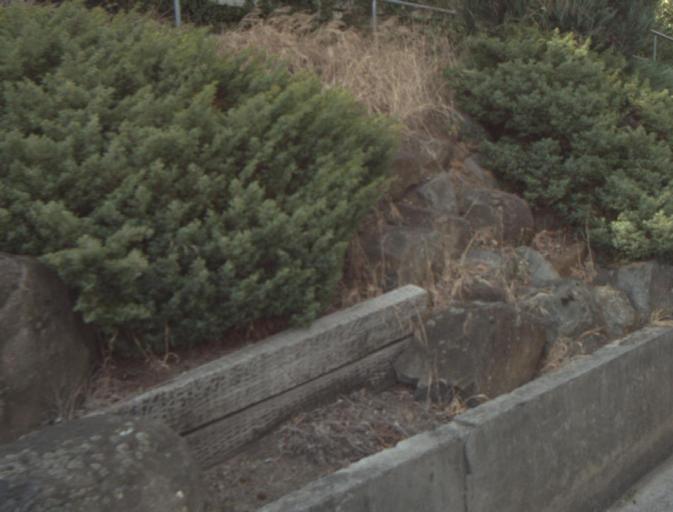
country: AU
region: Tasmania
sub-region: Launceston
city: Newstead
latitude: -41.4612
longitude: 147.1967
